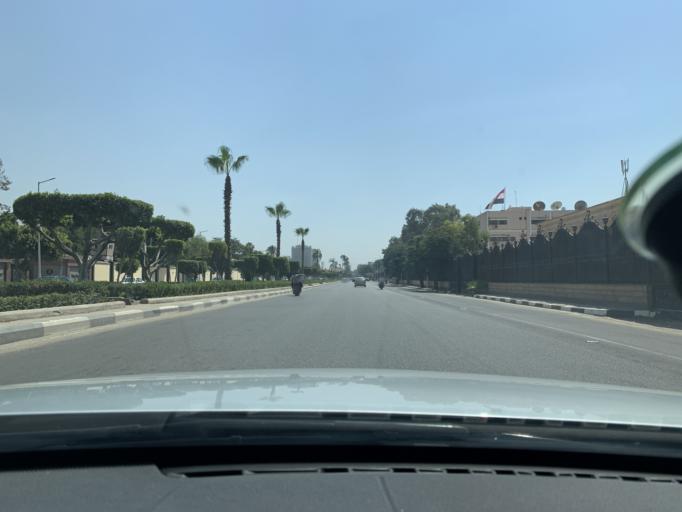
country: EG
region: Muhafazat al Qahirah
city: Cairo
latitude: 30.0819
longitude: 31.2933
